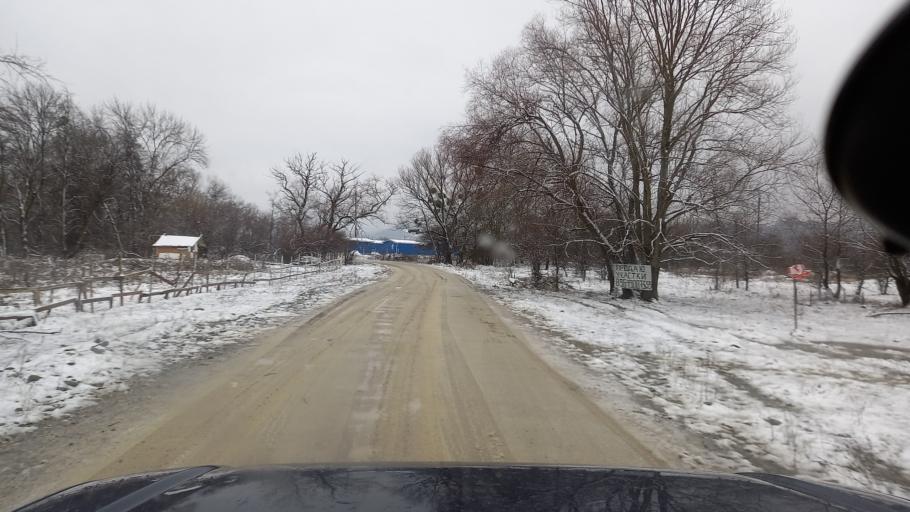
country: RU
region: Adygeya
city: Kamennomostskiy
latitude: 44.2311
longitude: 40.1877
